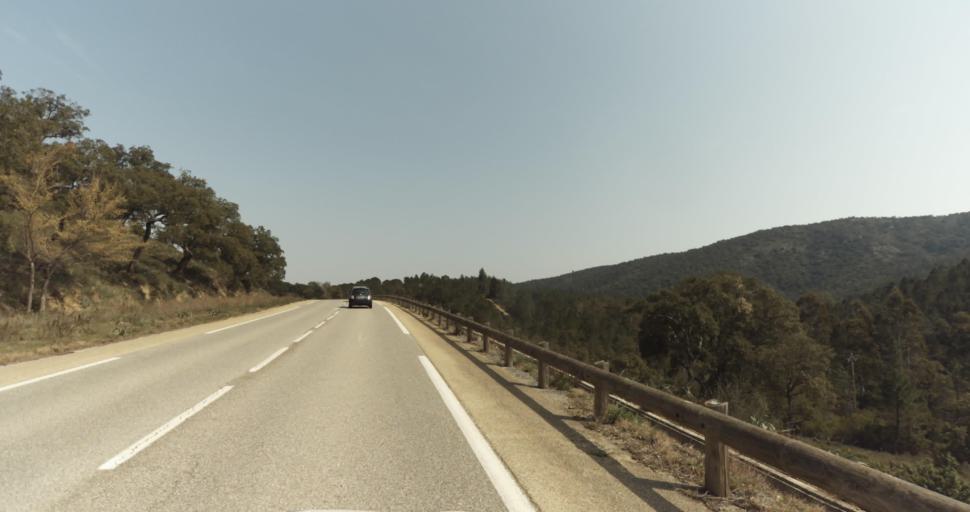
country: FR
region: Provence-Alpes-Cote d'Azur
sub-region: Departement du Var
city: Le Lavandou
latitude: 43.1893
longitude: 6.3679
